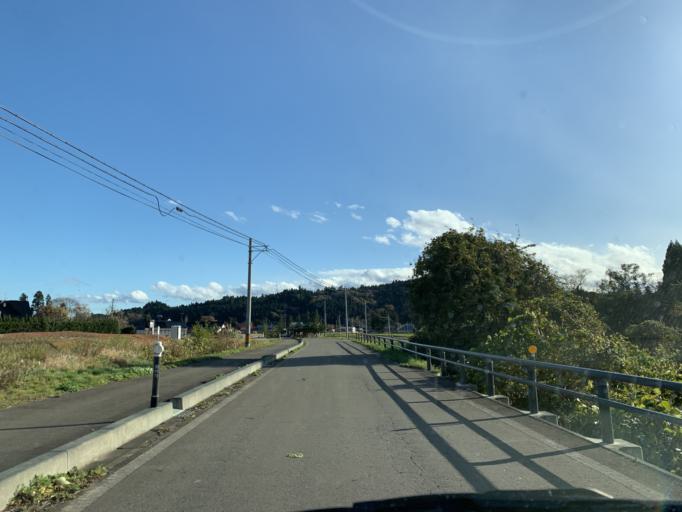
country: JP
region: Iwate
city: Ichinoseki
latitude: 39.0128
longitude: 141.0954
